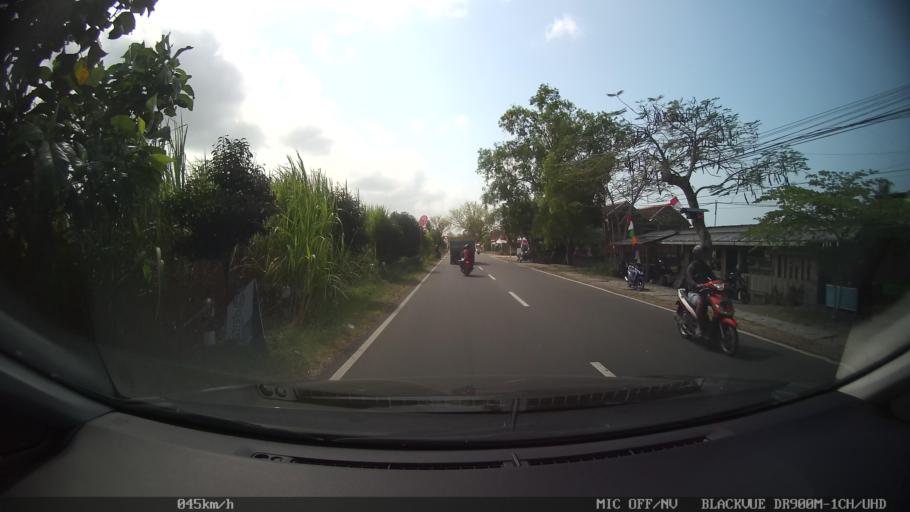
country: ID
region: Daerah Istimewa Yogyakarta
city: Srandakan
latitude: -7.8947
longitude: 110.1486
